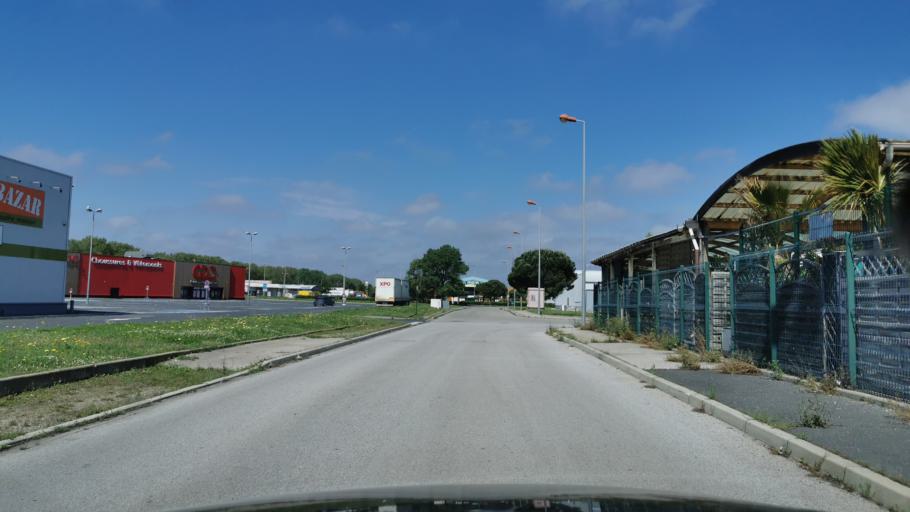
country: FR
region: Languedoc-Roussillon
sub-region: Departement de l'Aude
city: Narbonne
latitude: 43.1754
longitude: 3.0292
